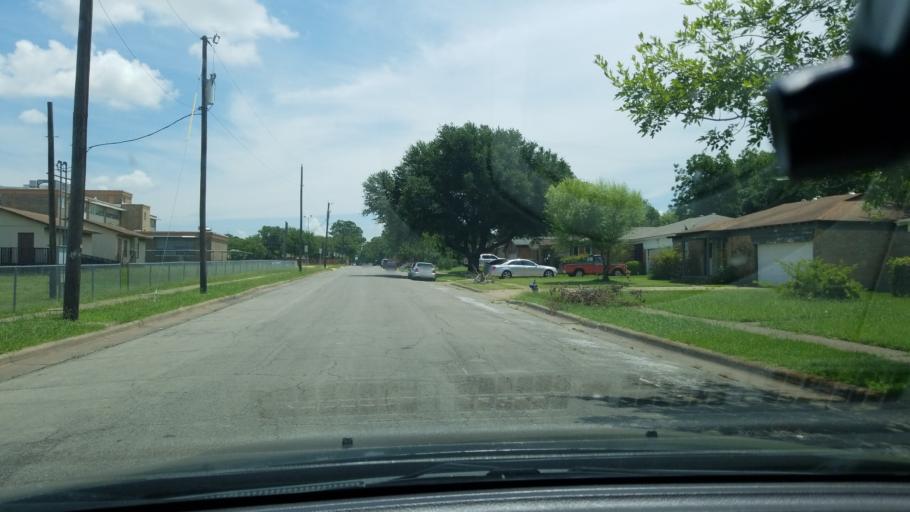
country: US
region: Texas
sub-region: Dallas County
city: Balch Springs
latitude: 32.7400
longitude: -96.6506
